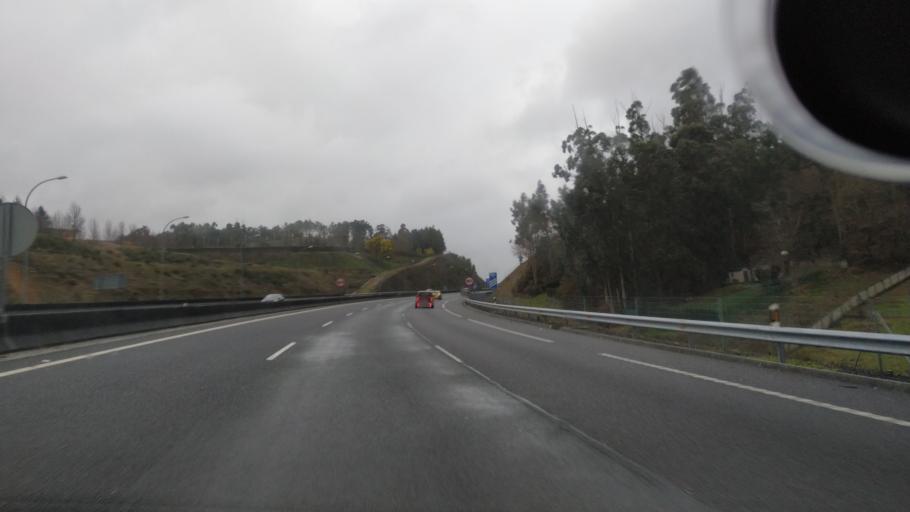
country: ES
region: Galicia
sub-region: Provincia da Coruna
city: Santiago de Compostela
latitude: 42.8479
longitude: -8.5330
